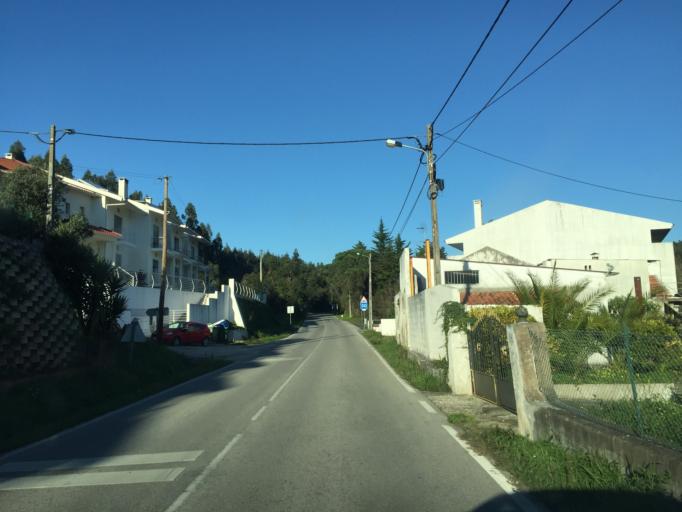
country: PT
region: Coimbra
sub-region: Figueira da Foz
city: Alhadas
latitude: 40.1684
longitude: -8.8063
